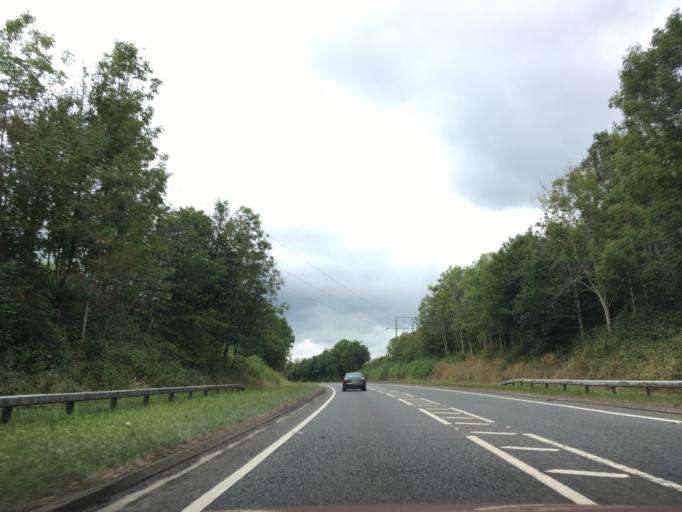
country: GB
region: Wales
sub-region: Carmarthenshire
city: Whitland
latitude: 51.8255
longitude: -4.6170
